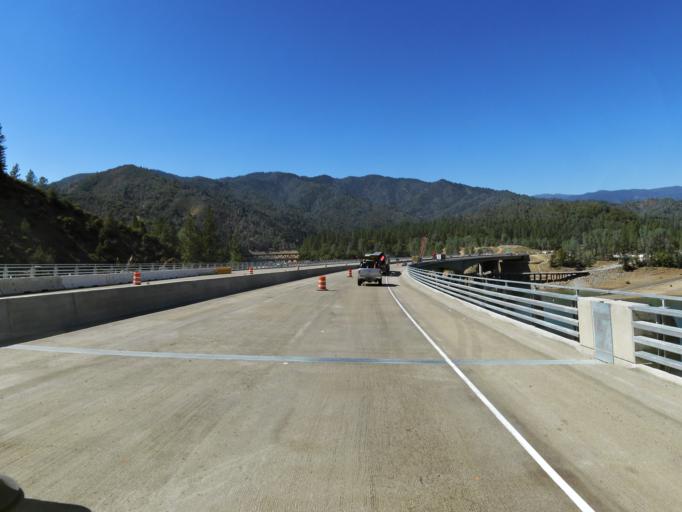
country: US
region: California
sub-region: Shasta County
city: Central Valley (historical)
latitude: 40.8792
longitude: -122.3780
